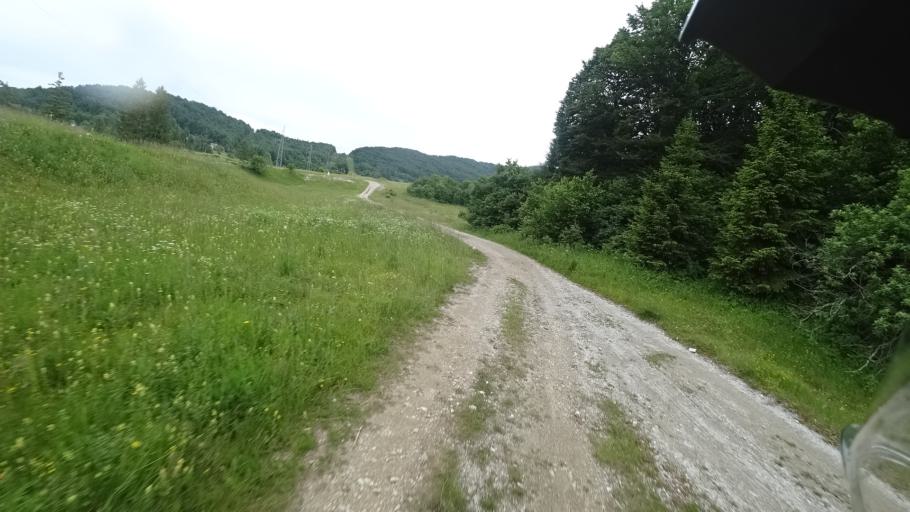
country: HR
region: Primorsko-Goranska
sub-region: Grad Delnice
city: Delnice
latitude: 45.3841
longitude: 14.8469
